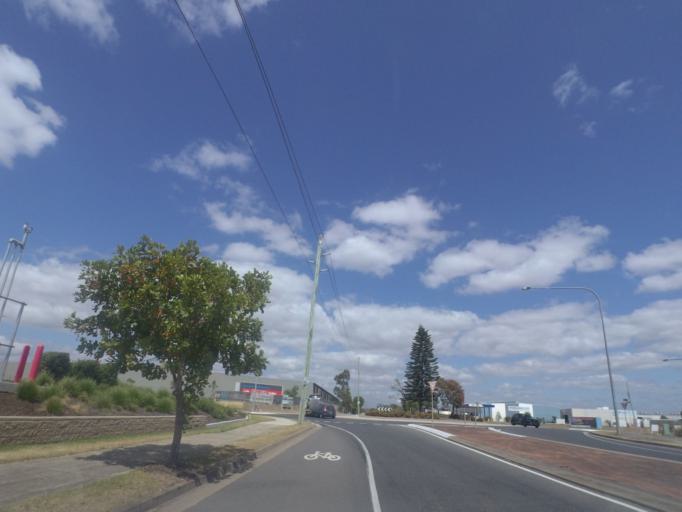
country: AU
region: Queensland
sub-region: Ipswich
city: Bundamba
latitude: -27.5891
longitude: 152.8209
